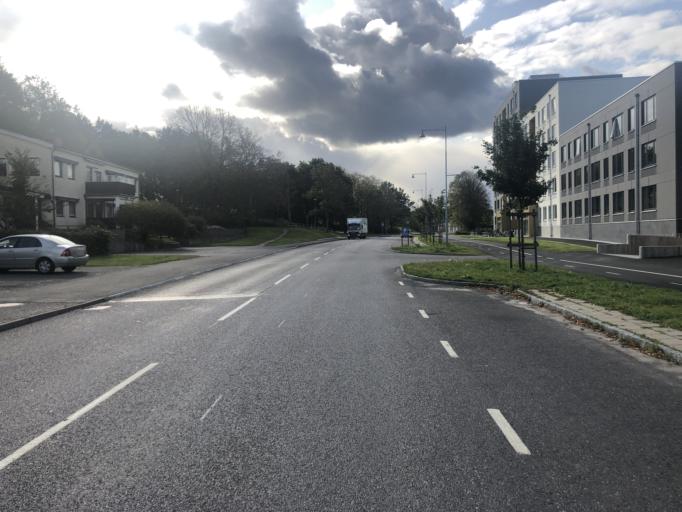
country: SE
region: Vaestra Goetaland
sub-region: Molndal
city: Moelndal
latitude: 57.6531
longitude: 12.0059
